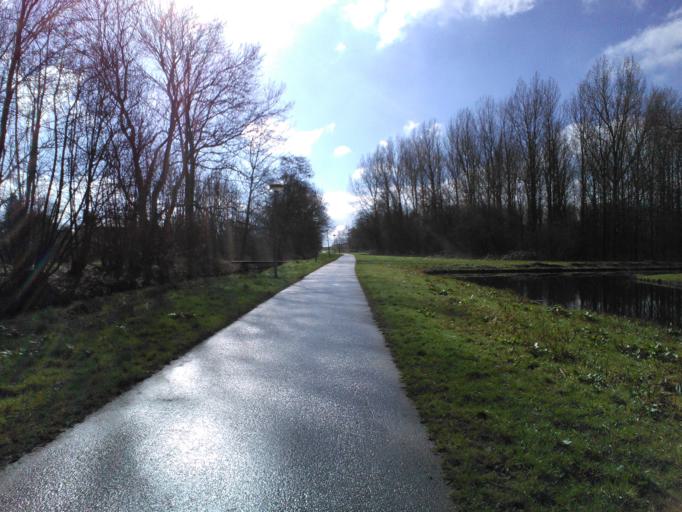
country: NL
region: South Holland
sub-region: Gemeente Delft
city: Delft
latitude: 51.9888
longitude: 4.3326
